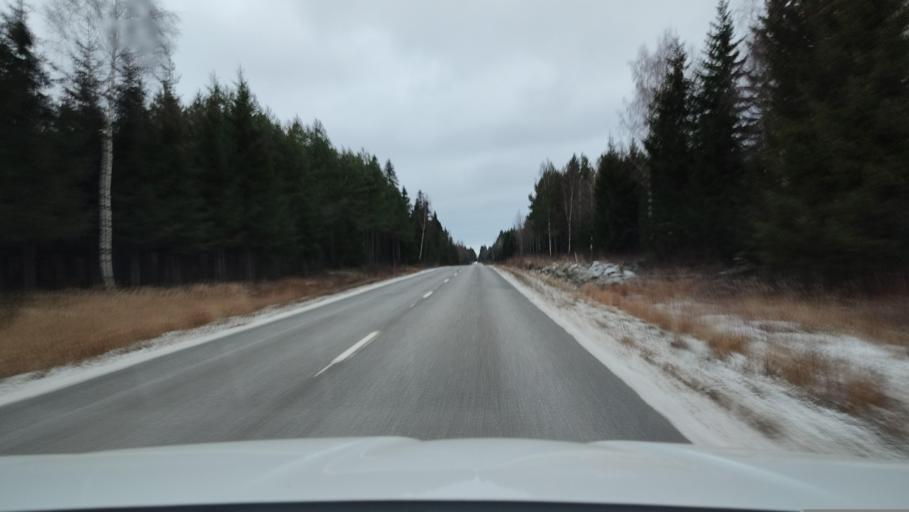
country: FI
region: Ostrobothnia
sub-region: Vaasa
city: Replot
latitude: 63.2587
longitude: 21.3648
